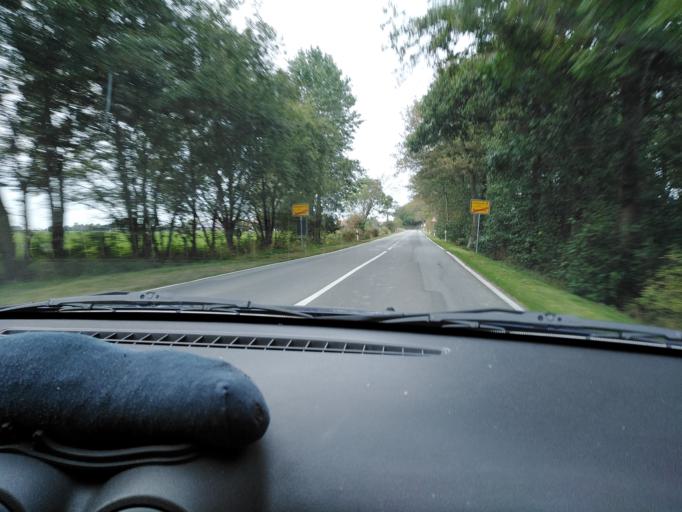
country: DE
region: Lower Saxony
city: Jever
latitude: 53.6756
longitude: 7.8649
